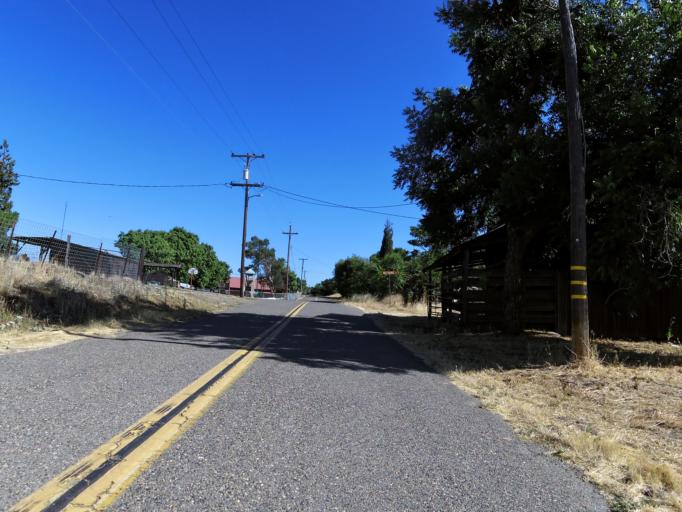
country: US
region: California
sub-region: Merced County
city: Planada
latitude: 37.5005
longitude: -120.2377
